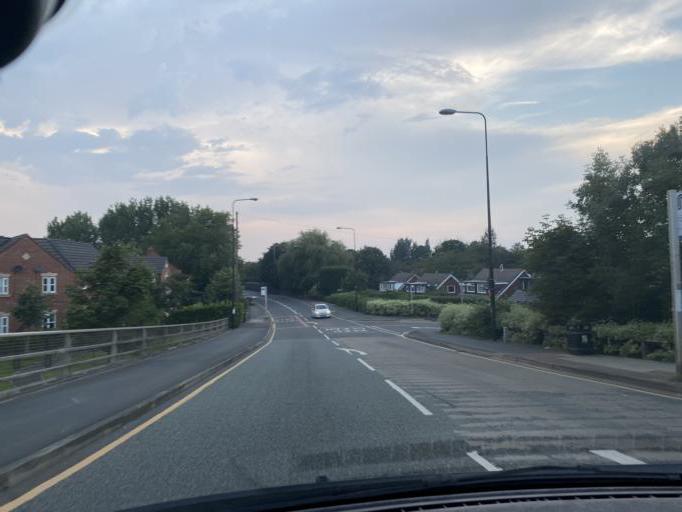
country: GB
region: England
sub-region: Borough of Tameside
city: Droylsden
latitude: 53.4723
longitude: -2.1341
